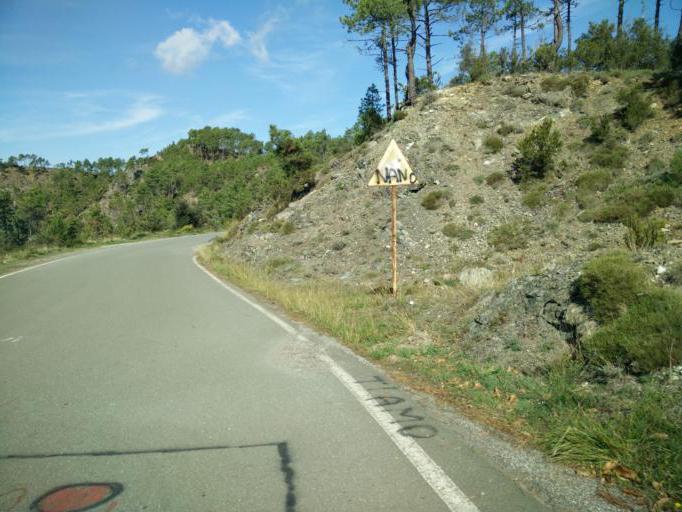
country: IT
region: Liguria
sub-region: Provincia di La Spezia
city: Framura
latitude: 44.2349
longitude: 9.5836
